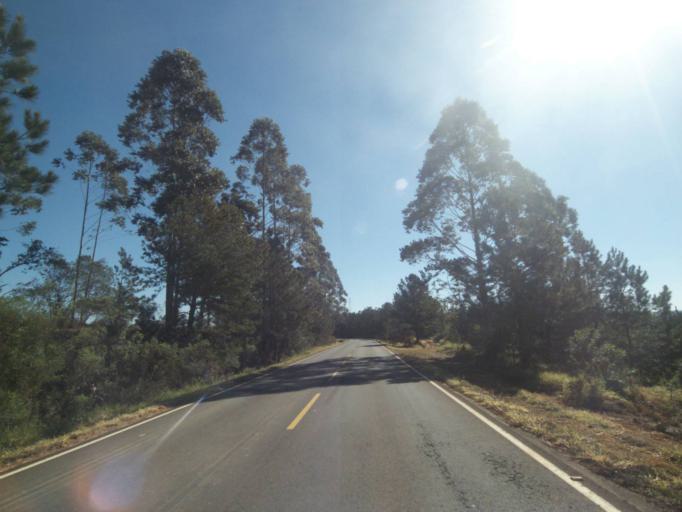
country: BR
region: Parana
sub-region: Tibagi
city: Tibagi
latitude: -24.4532
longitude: -50.5452
